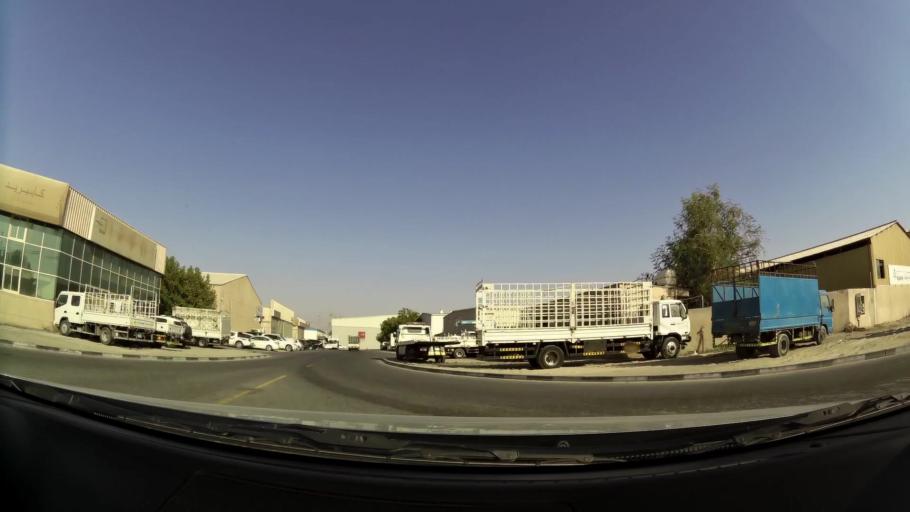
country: AE
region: Dubai
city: Dubai
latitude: 25.1173
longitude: 55.2354
